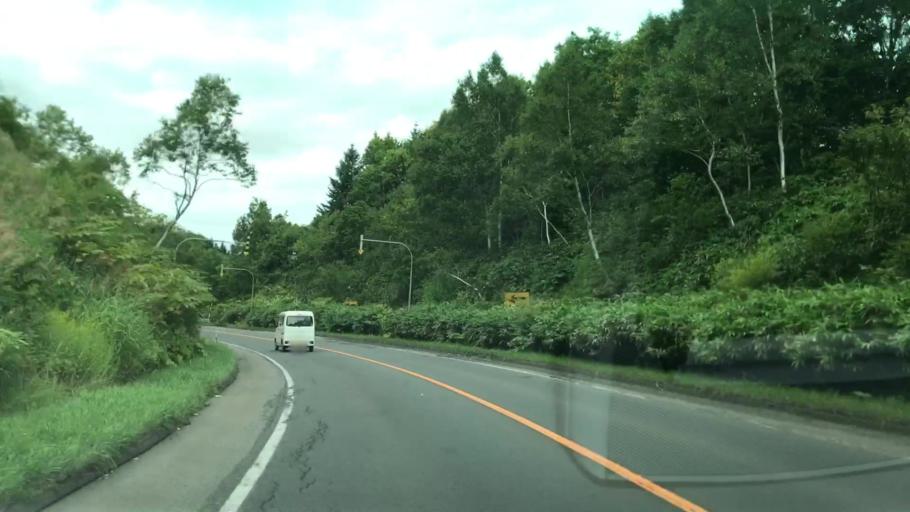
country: JP
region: Hokkaido
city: Niseko Town
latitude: 42.9270
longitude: 140.7168
